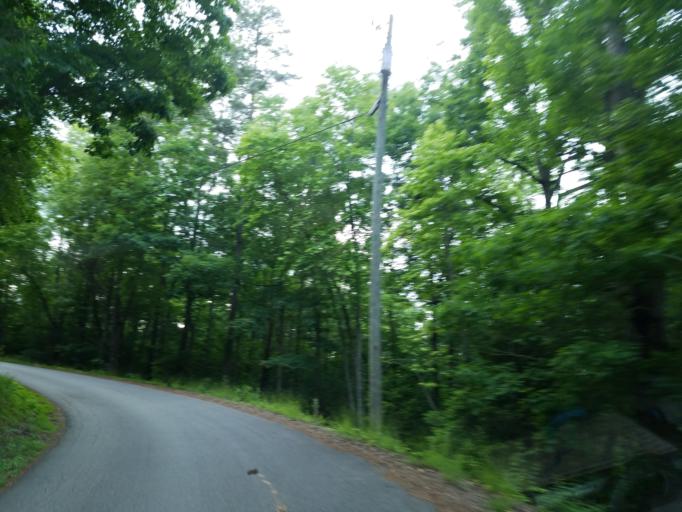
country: US
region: Georgia
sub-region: Lumpkin County
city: Dahlonega
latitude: 34.5972
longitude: -84.0832
